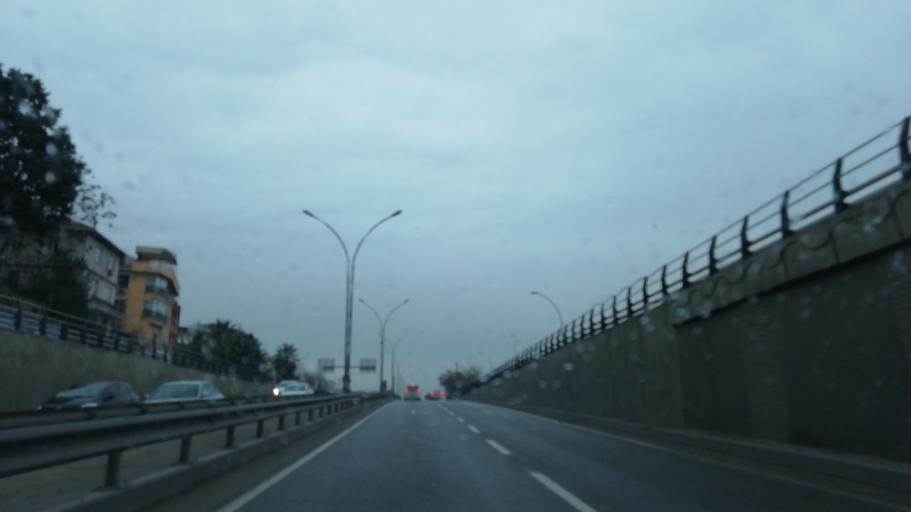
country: TR
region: Kocaeli
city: Izmit
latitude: 40.7636
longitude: 29.9153
